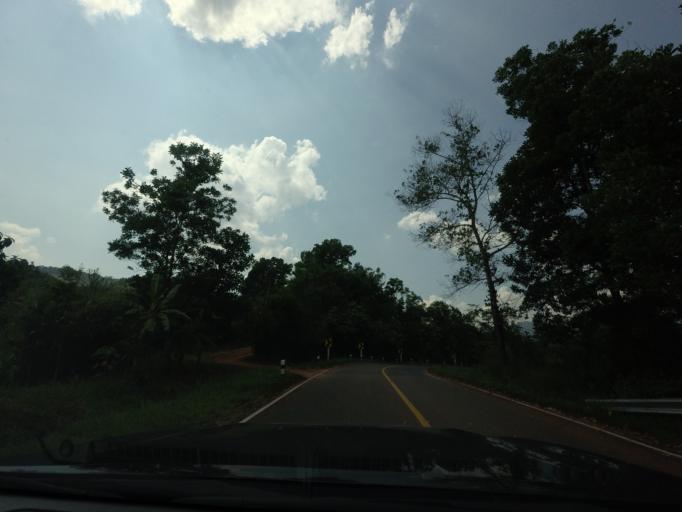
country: TH
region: Nan
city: Bo Kluea
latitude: 19.0107
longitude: 101.1958
